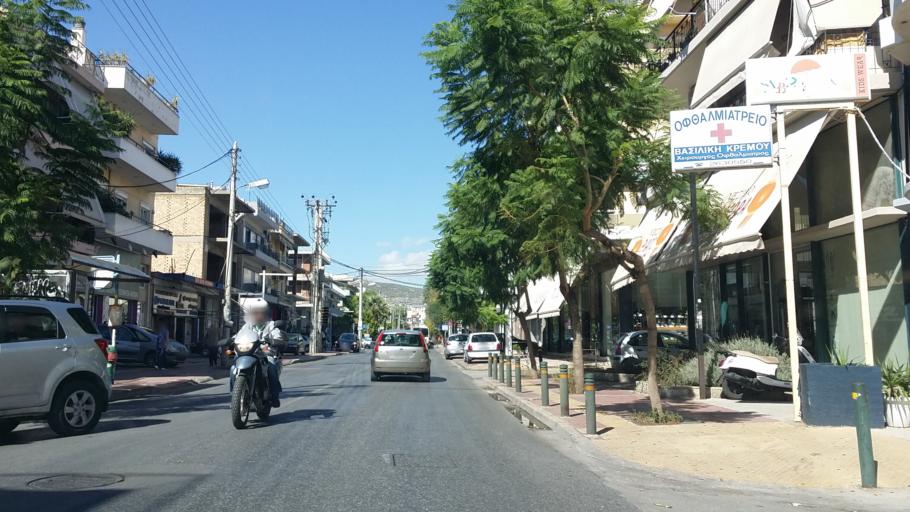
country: GR
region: Attica
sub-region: Nomarchia Athinas
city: Agioi Anargyroi
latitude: 38.0287
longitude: 23.7159
